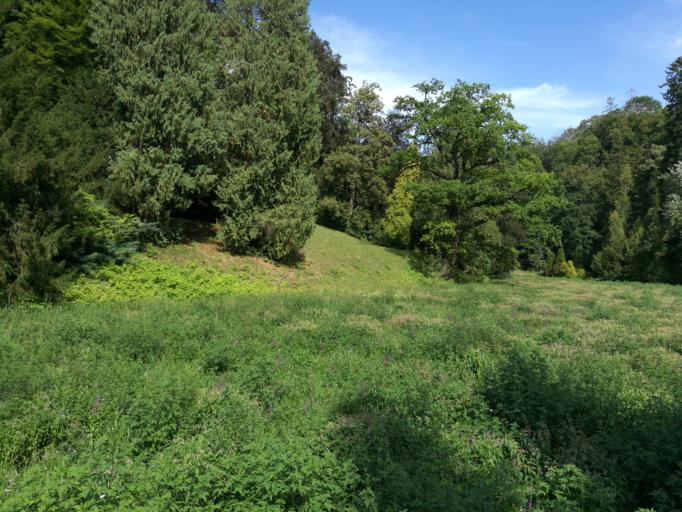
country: CZ
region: Kralovehradecky
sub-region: Okres Rychnov nad Kneznou
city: Opocno
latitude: 50.2639
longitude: 16.1145
